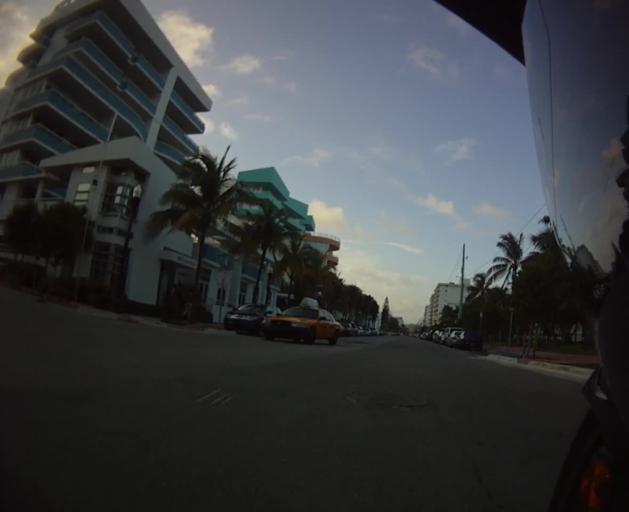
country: US
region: Florida
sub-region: Miami-Dade County
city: Miami Beach
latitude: 25.7708
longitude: -80.1327
